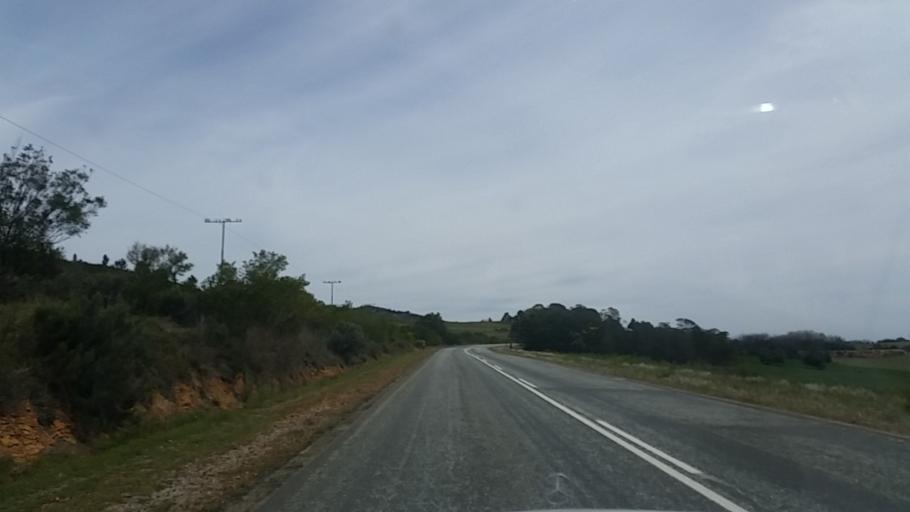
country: ZA
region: Western Cape
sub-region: Eden District Municipality
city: Knysna
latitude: -33.7745
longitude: 22.9106
